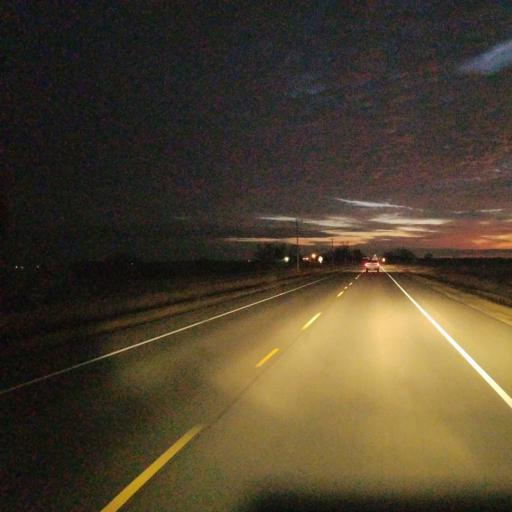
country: US
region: Illinois
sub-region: Peoria County
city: Hanna City
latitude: 40.6974
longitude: -89.8589
